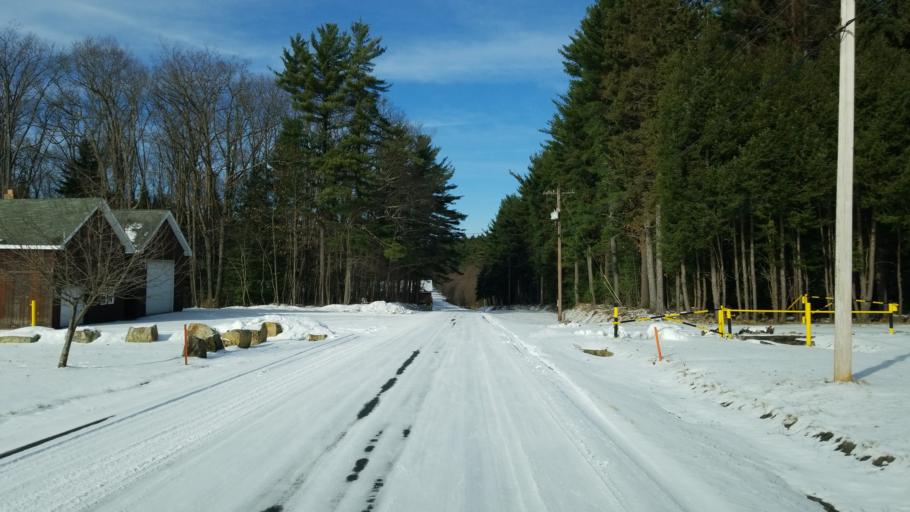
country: US
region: Pennsylvania
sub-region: Clearfield County
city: Clearfield
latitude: 41.1172
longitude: -78.5289
